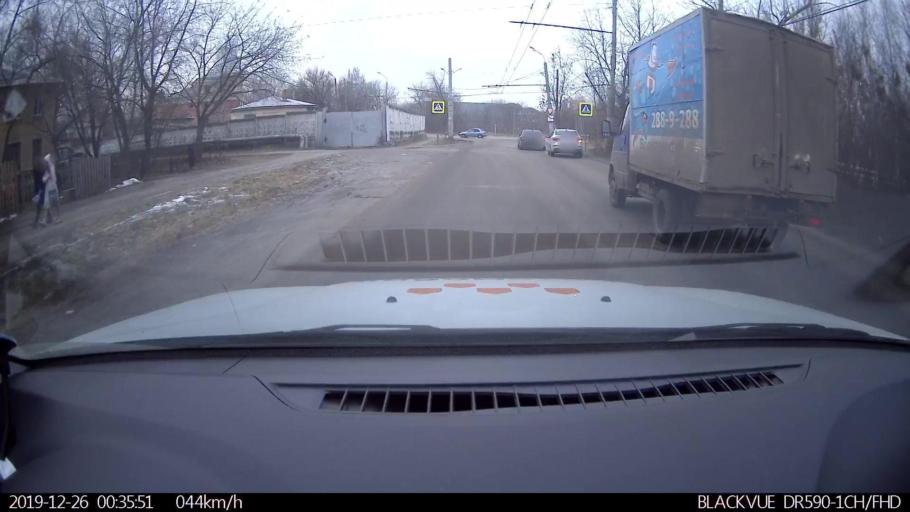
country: RU
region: Nizjnij Novgorod
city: Nizhniy Novgorod
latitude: 56.2929
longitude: 43.9120
